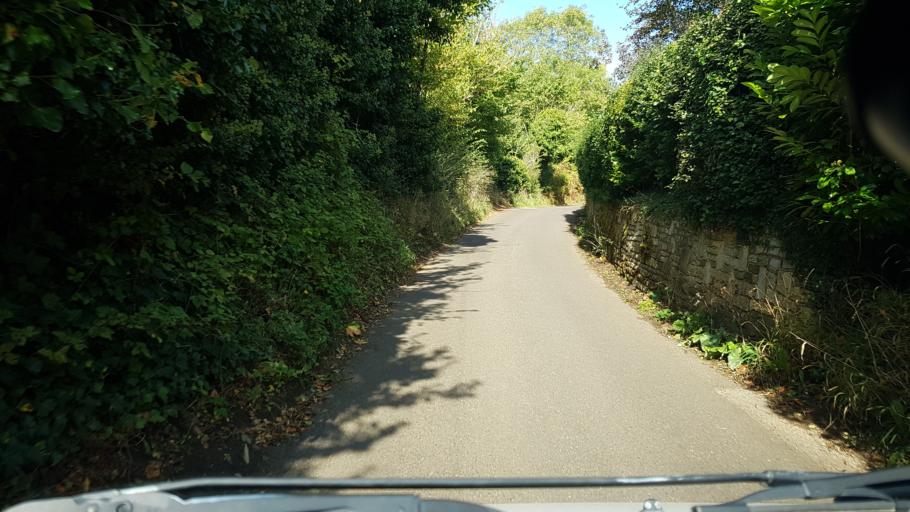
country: GB
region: England
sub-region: Surrey
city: Guildford
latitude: 51.2198
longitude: -0.5959
